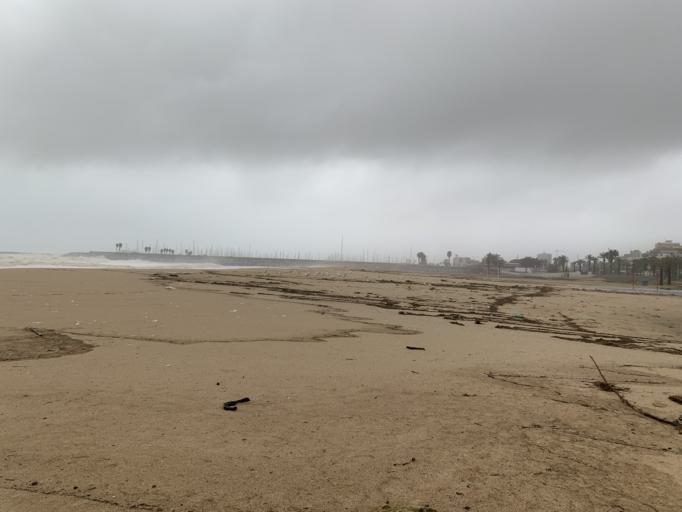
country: ES
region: Catalonia
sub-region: Provincia de Barcelona
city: Mataro
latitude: 41.5350
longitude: 2.4502
